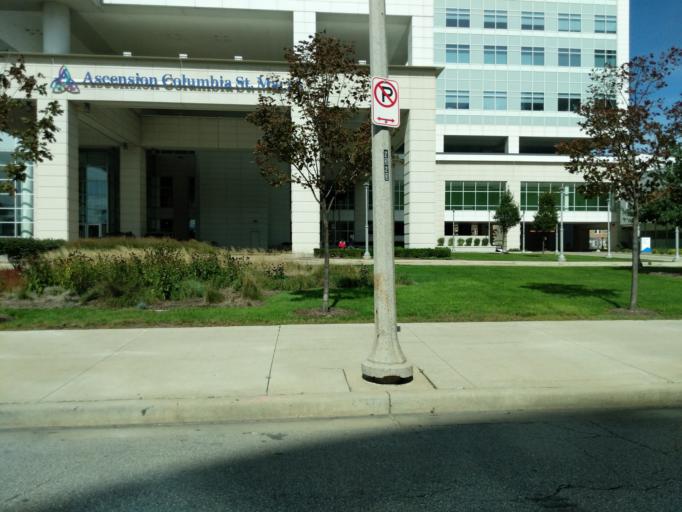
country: US
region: Wisconsin
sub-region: Milwaukee County
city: Shorewood
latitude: 43.0604
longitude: -87.8801
